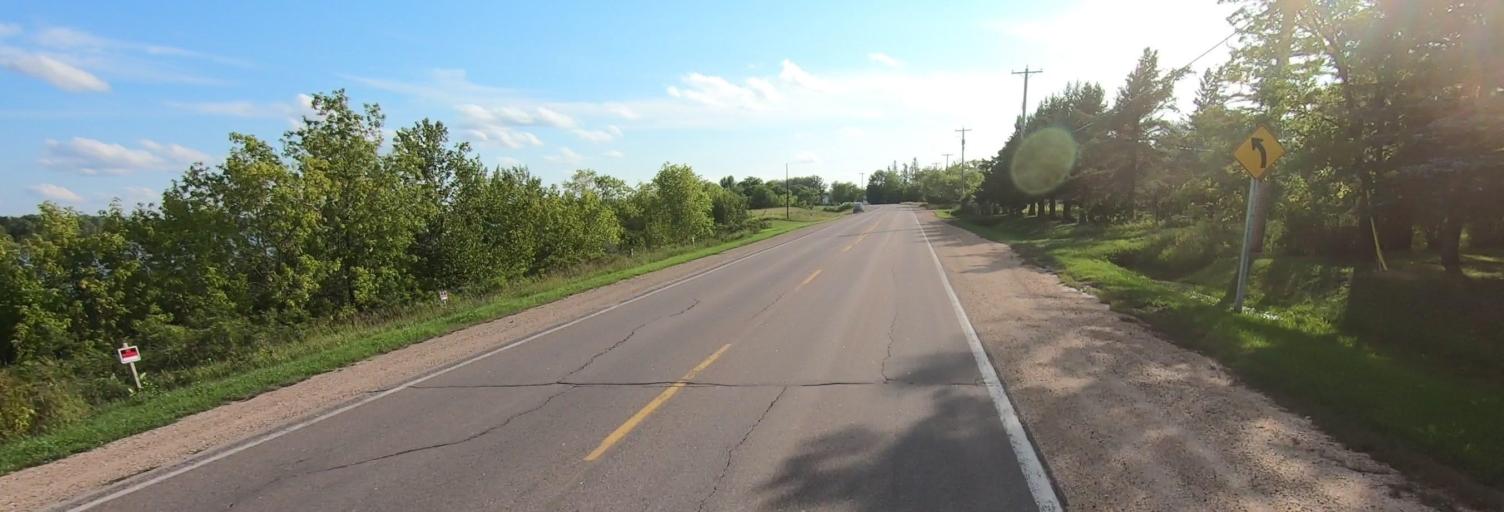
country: CA
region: Manitoba
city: Selkirk
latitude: 50.1776
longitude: -96.8550
